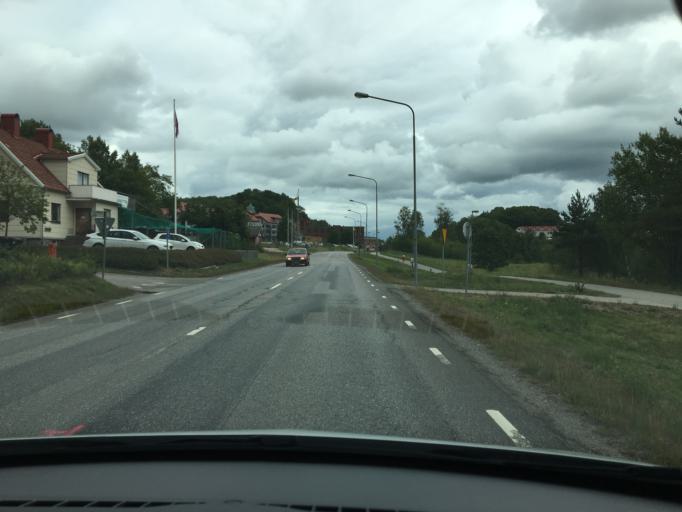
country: SE
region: Vaestra Goetaland
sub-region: Ale Kommun
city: Alafors
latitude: 57.9225
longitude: 12.0966
